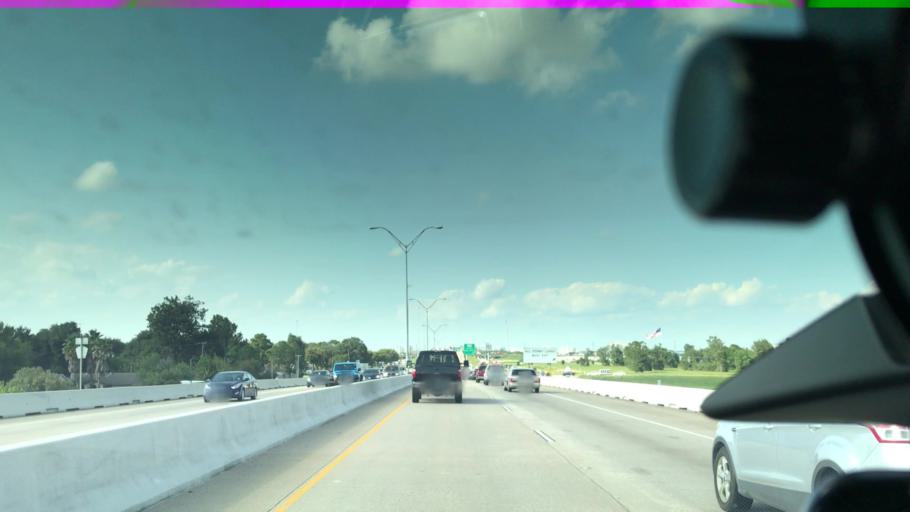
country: US
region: Texas
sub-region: Harris County
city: Deer Park
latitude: 29.7027
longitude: -95.1534
